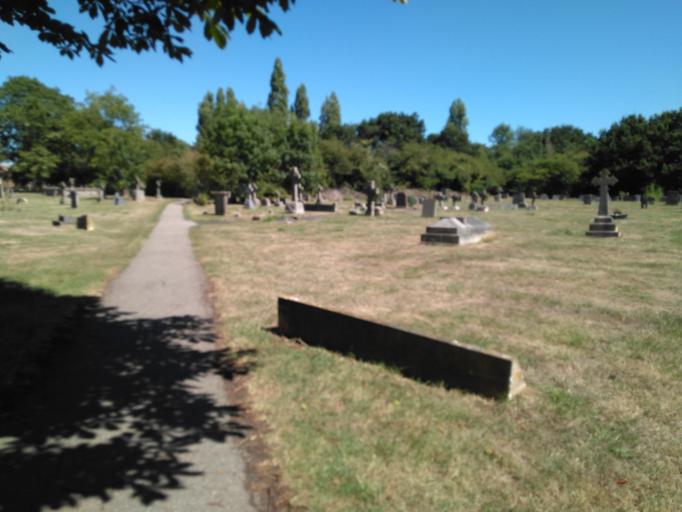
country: GB
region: England
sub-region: Kent
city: Tankerton
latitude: 51.3549
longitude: 1.0395
